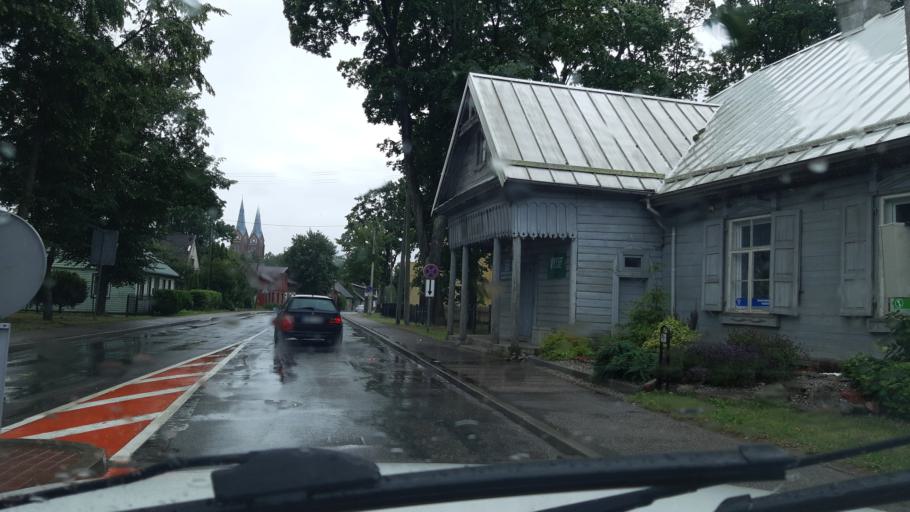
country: LT
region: Taurages apskritis
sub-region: Jurbarkas
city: Jurbarkas
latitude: 55.0790
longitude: 22.7605
